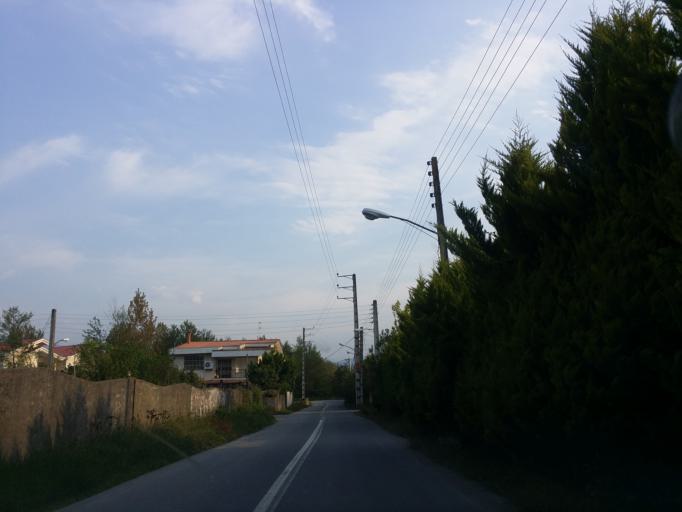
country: IR
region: Mazandaran
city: Chalus
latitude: 36.6856
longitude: 51.3723
